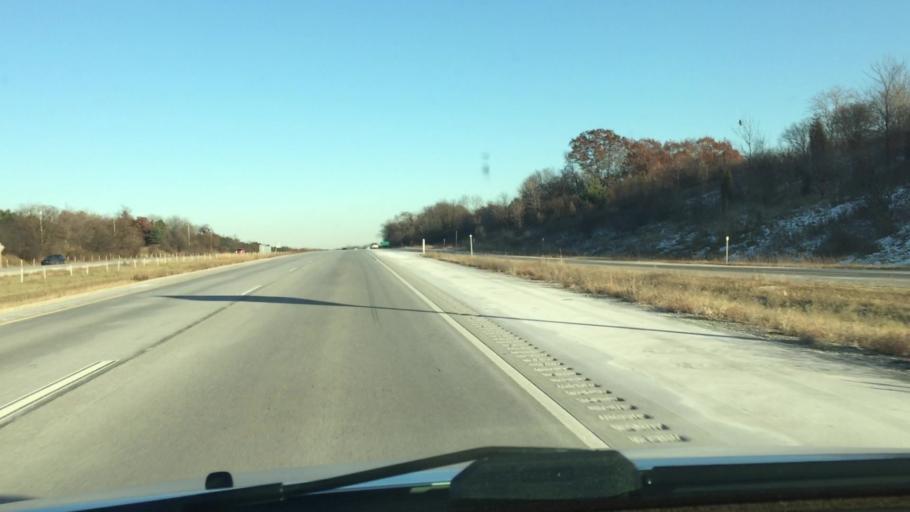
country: US
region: Wisconsin
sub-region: Waukesha County
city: Nashotah
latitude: 43.1017
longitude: -88.4000
